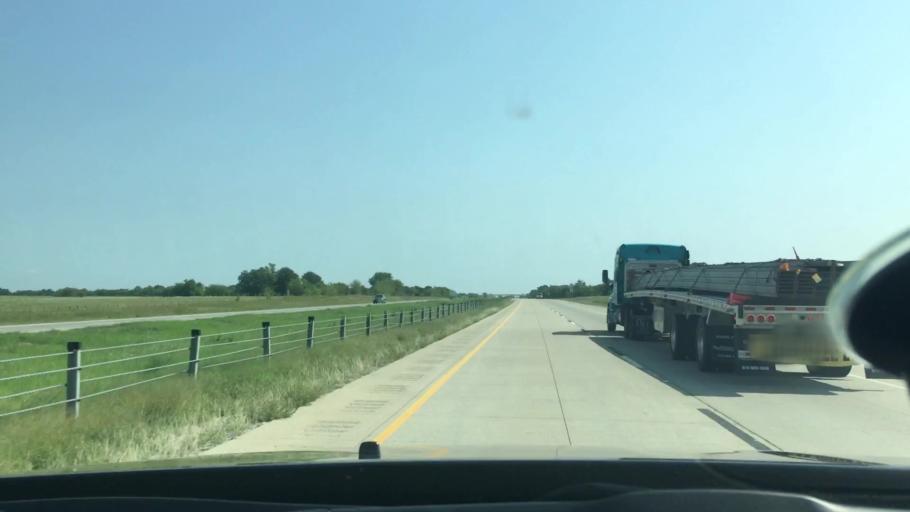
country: US
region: Oklahoma
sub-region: Bryan County
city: Durant
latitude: 34.0995
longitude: -96.3142
